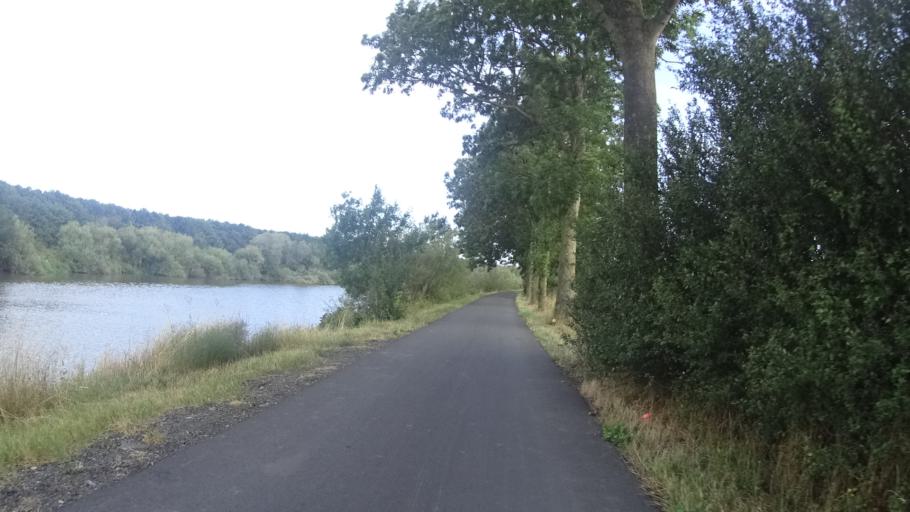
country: BE
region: Flanders
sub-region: Provincie West-Vlaanderen
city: Ieper
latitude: 50.9209
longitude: 2.8435
